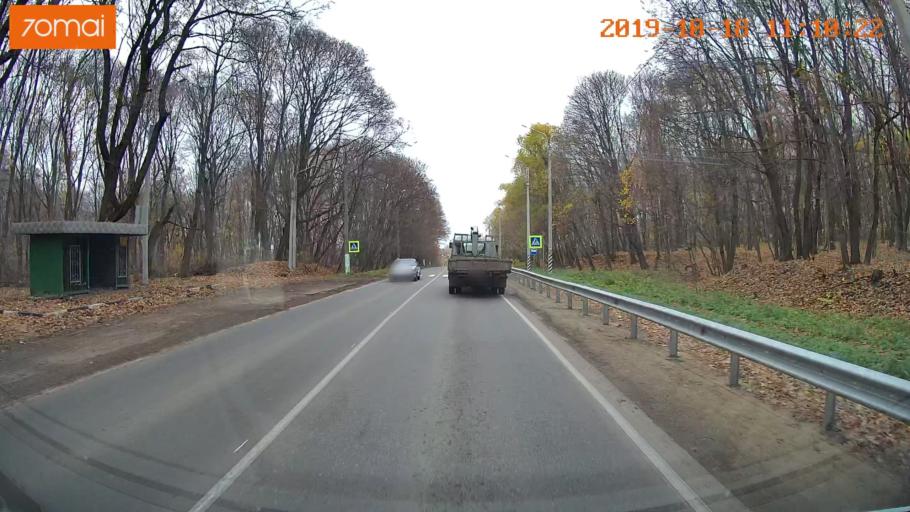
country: RU
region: Tula
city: Kimovsk
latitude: 53.9549
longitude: 38.5390
